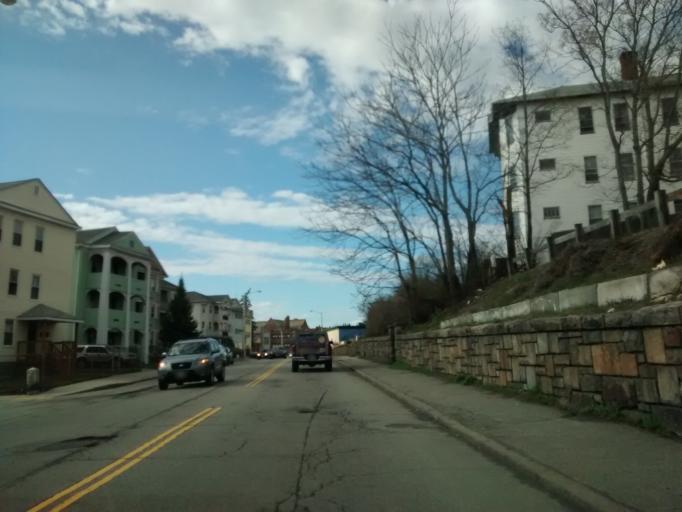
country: US
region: Massachusetts
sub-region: Worcester County
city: Sunderland
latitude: 42.2528
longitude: -71.7827
